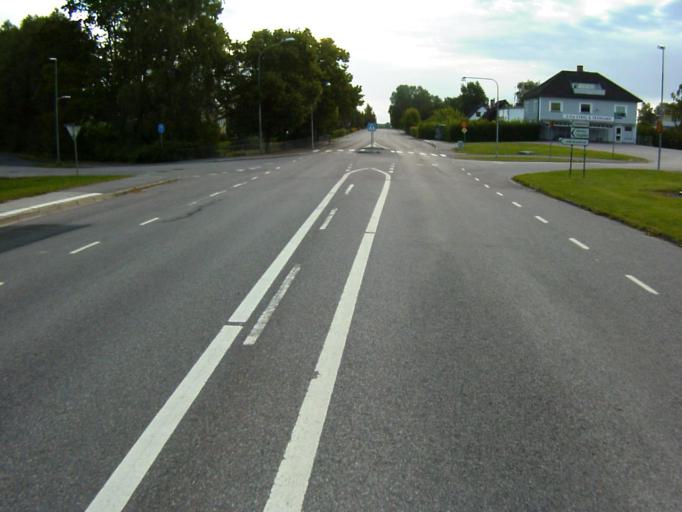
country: SE
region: Soedermanland
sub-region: Eskilstuna Kommun
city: Hallbybrunn
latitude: 59.3752
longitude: 16.4496
